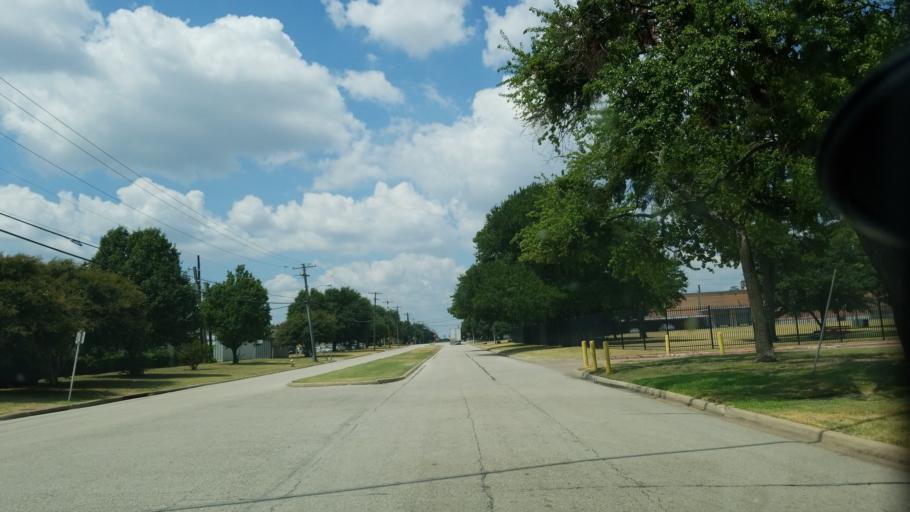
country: US
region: Texas
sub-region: Dallas County
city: Duncanville
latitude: 32.6872
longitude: -96.8887
